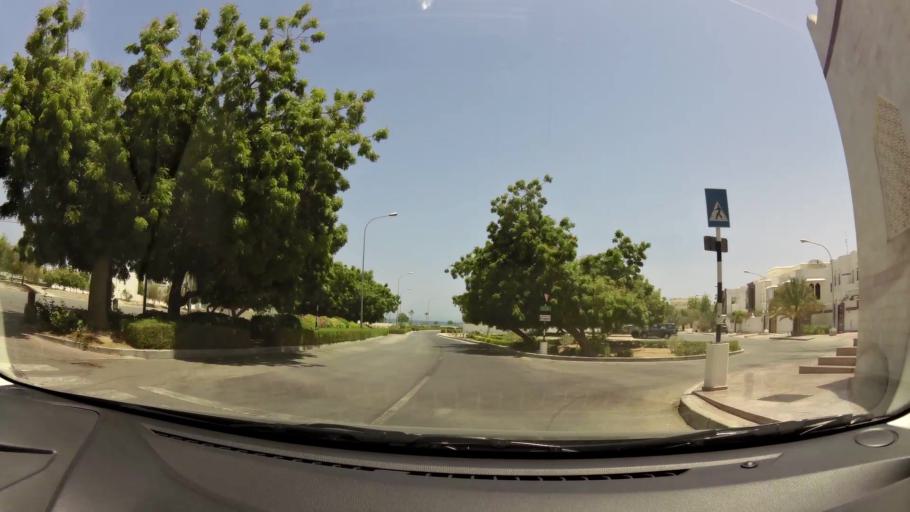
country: OM
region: Muhafazat Masqat
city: Bawshar
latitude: 23.6108
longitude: 58.4568
